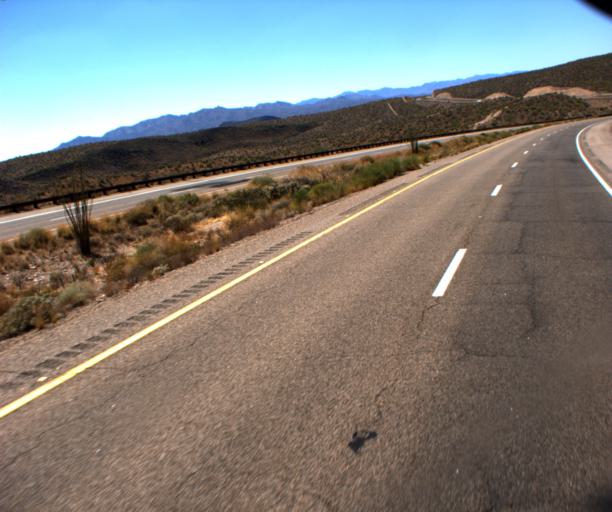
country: US
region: Arizona
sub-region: Yavapai County
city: Bagdad
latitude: 34.5734
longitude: -113.4880
